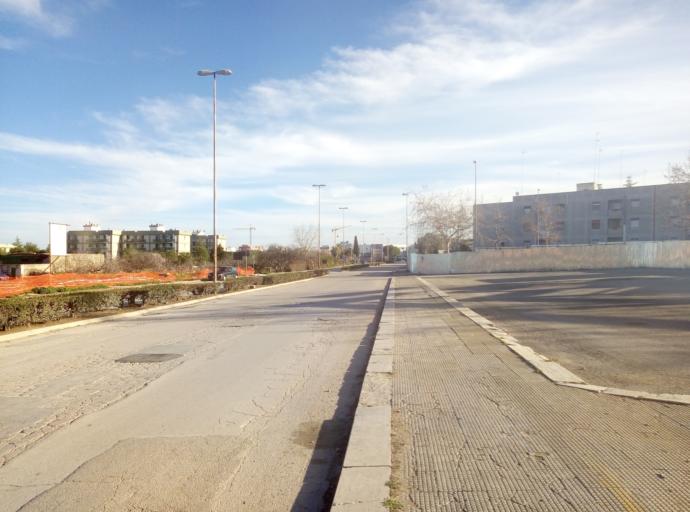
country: IT
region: Apulia
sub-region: Provincia di Bari
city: Ruvo di Puglia
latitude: 41.1193
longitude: 16.4915
